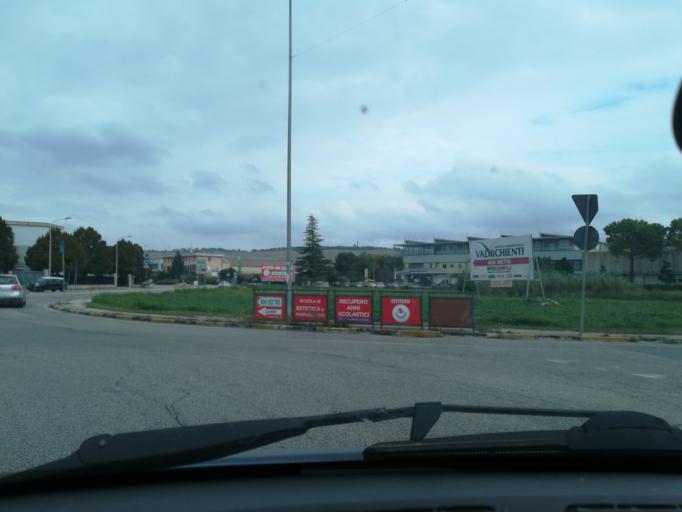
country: IT
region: The Marches
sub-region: Provincia di Macerata
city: Piediripa
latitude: 43.2755
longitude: 13.4998
